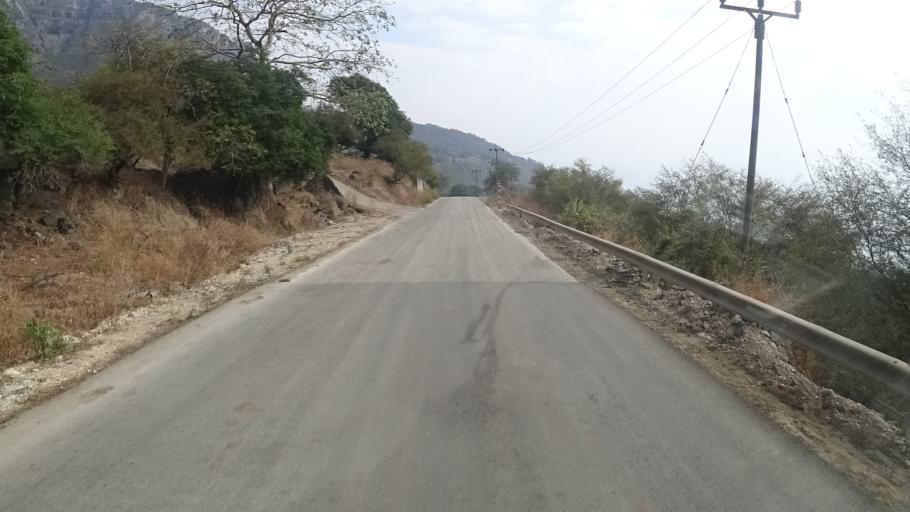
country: YE
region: Al Mahrah
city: Hawf
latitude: 16.7078
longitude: 53.2248
